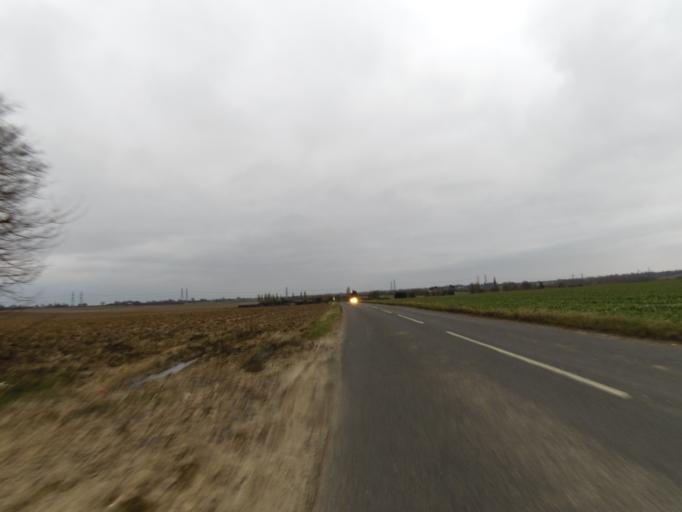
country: GB
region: England
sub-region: Suffolk
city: Ipswich
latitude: 52.1065
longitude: 1.1530
